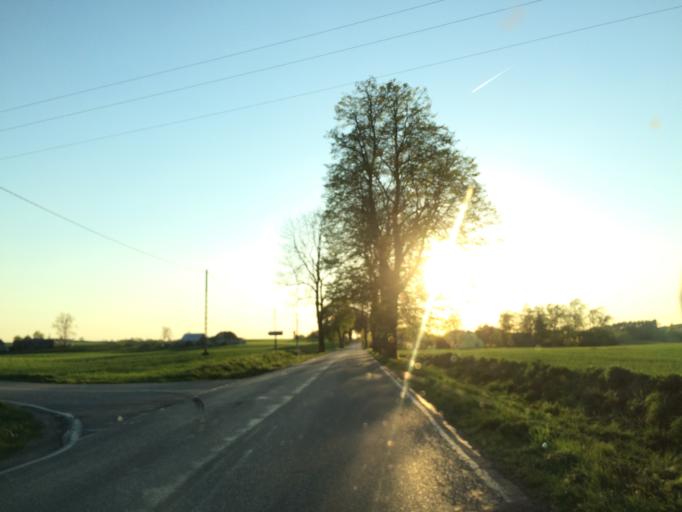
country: PL
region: Warmian-Masurian Voivodeship
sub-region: Powiat ilawski
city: Lubawa
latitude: 53.5063
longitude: 19.8527
